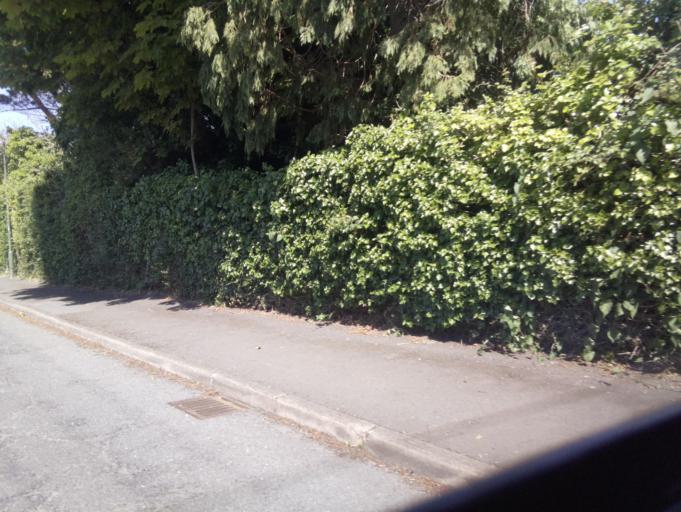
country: GB
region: England
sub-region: Borough of Torbay
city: Paignton
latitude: 50.4147
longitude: -3.5683
